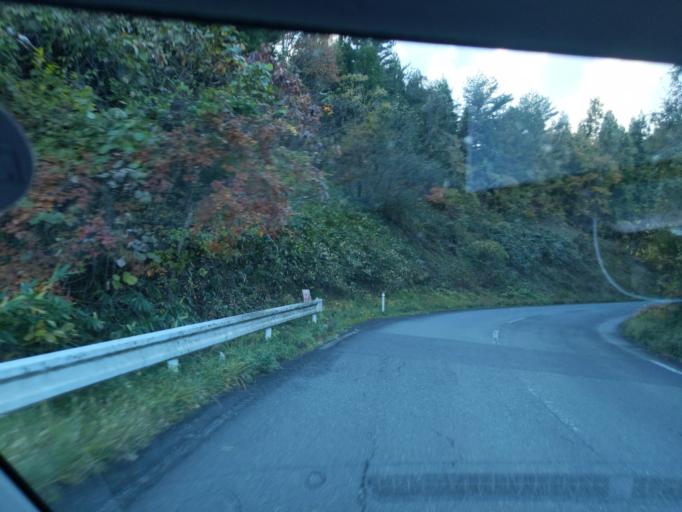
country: JP
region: Iwate
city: Mizusawa
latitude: 39.0501
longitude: 141.0397
